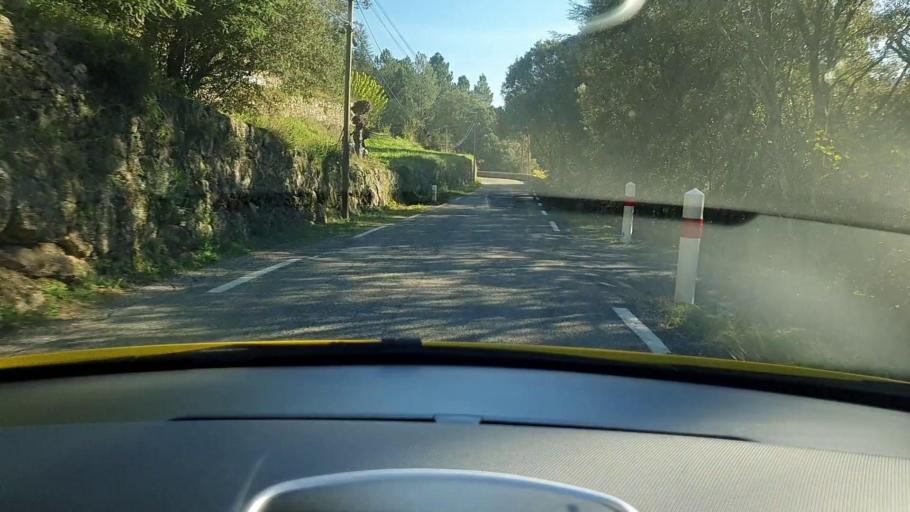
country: FR
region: Languedoc-Roussillon
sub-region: Departement du Gard
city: Lasalle
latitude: 44.0555
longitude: 3.8394
